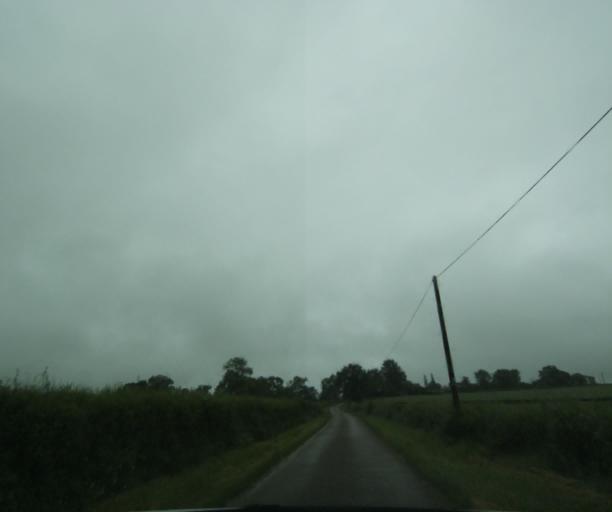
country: FR
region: Bourgogne
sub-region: Departement de Saone-et-Loire
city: Charolles
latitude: 46.4678
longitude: 4.2265
